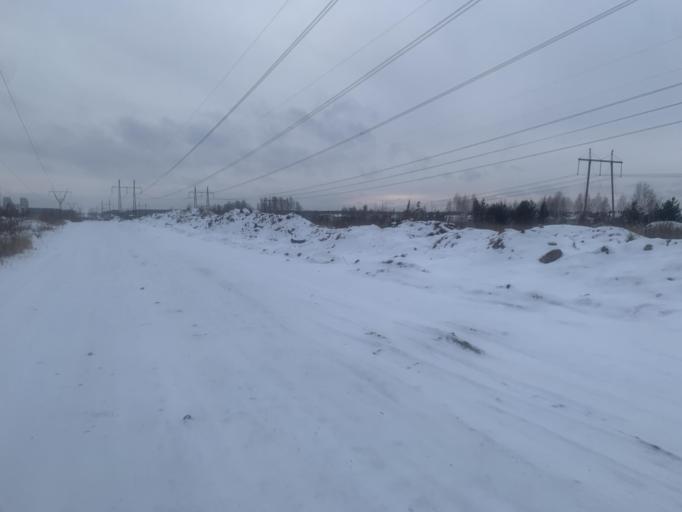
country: RU
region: Chelyabinsk
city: Roshchino
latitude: 55.1919
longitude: 61.2594
